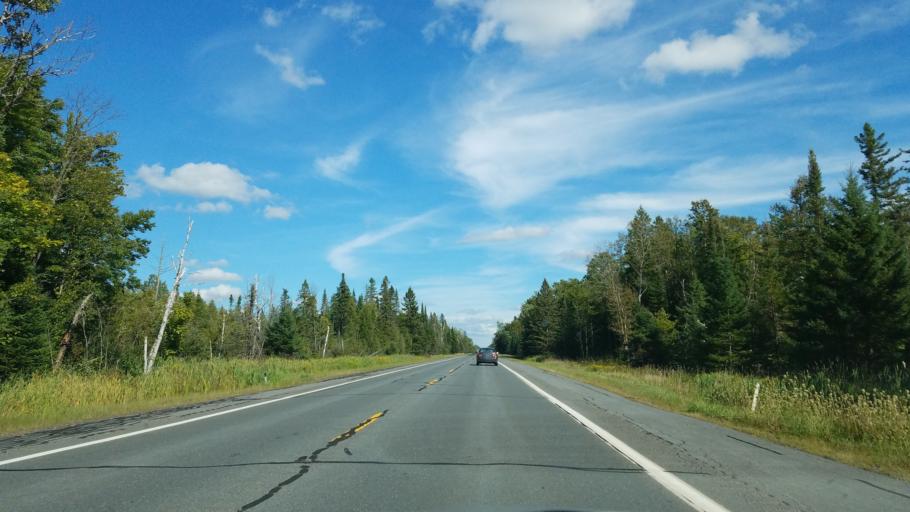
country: US
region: Michigan
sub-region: Baraga County
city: L'Anse
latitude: 46.5788
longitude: -88.4307
